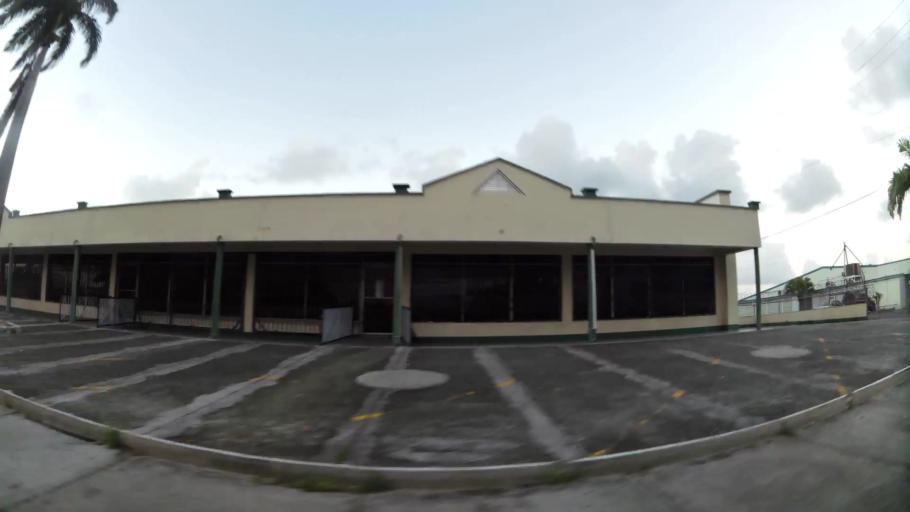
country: AG
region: Saint John
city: Saint John's
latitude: 17.1241
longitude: -61.8319
